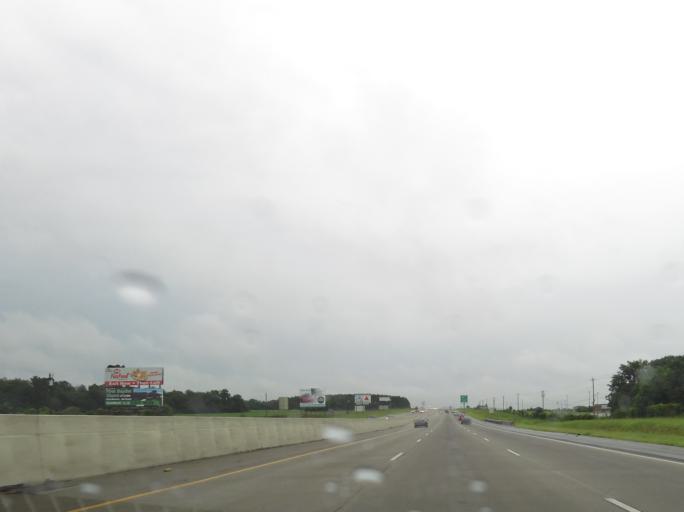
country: US
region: Georgia
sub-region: Crisp County
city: Cordele
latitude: 31.9483
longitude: -83.7497
